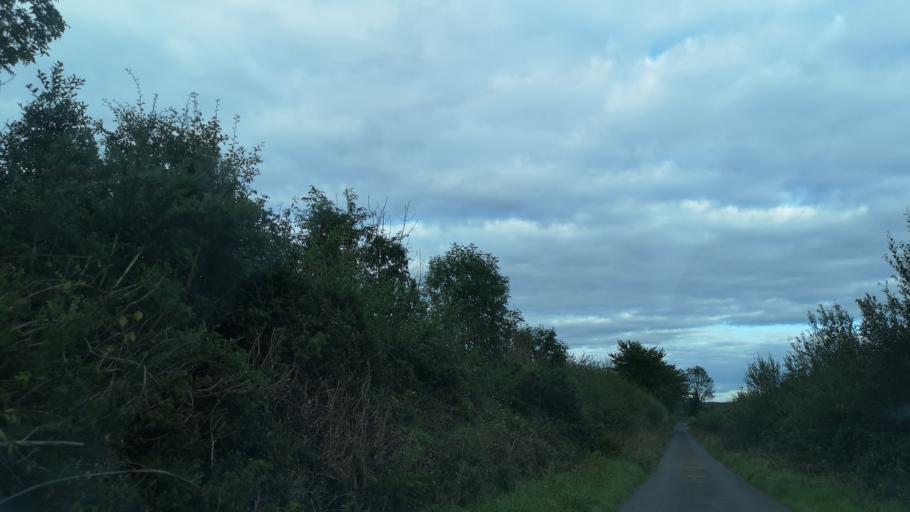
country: IE
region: Connaught
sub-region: County Galway
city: Loughrea
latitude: 53.1491
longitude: -8.5161
